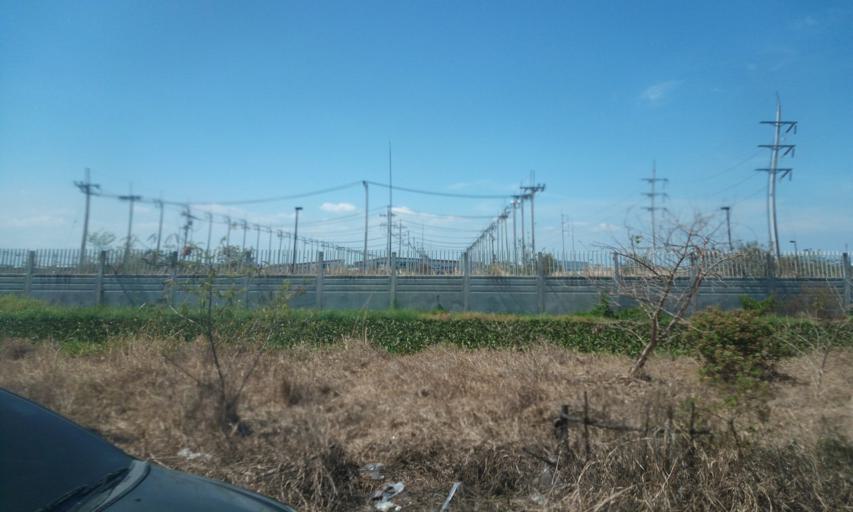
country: TH
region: Samut Prakan
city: Bang Bo District
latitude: 13.5556
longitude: 100.7724
